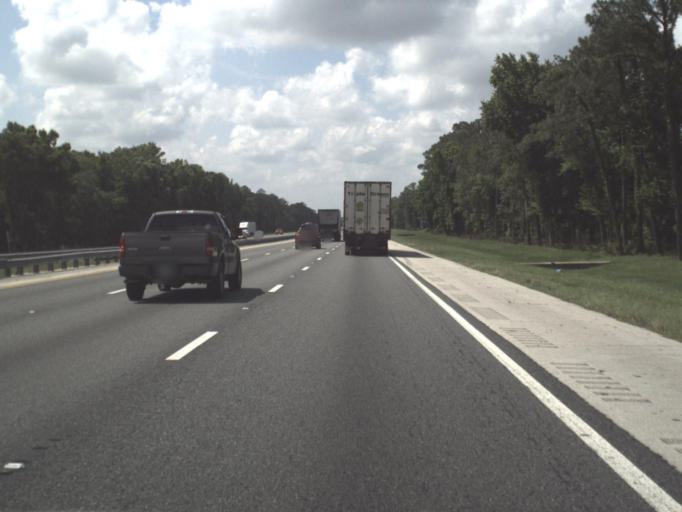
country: US
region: Florida
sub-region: Saint Johns County
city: Saint Augustine
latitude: 29.9337
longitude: -81.4235
